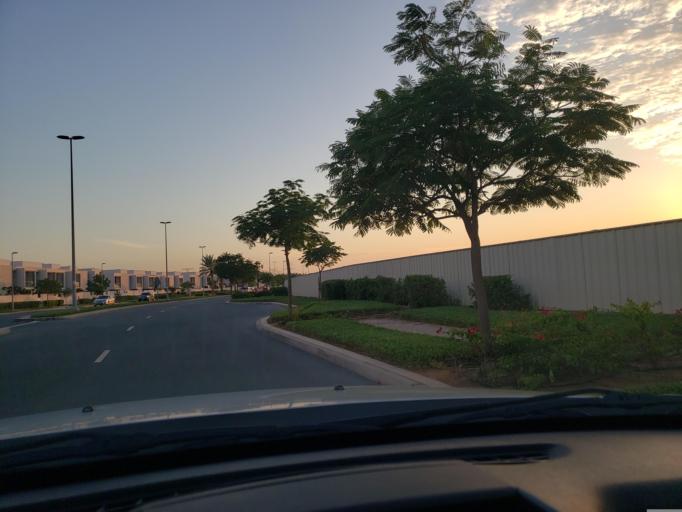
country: AE
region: Dubai
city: Dubai
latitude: 25.0168
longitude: 55.2675
